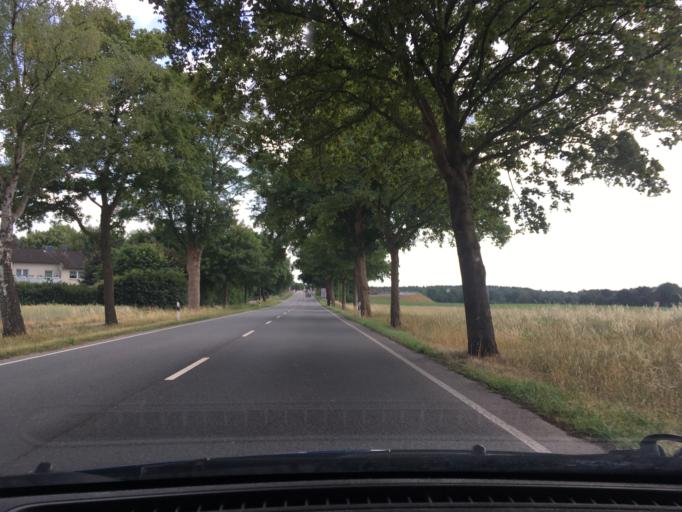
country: DE
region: Lower Saxony
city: Kakenstorf
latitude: 53.3073
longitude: 9.8016
